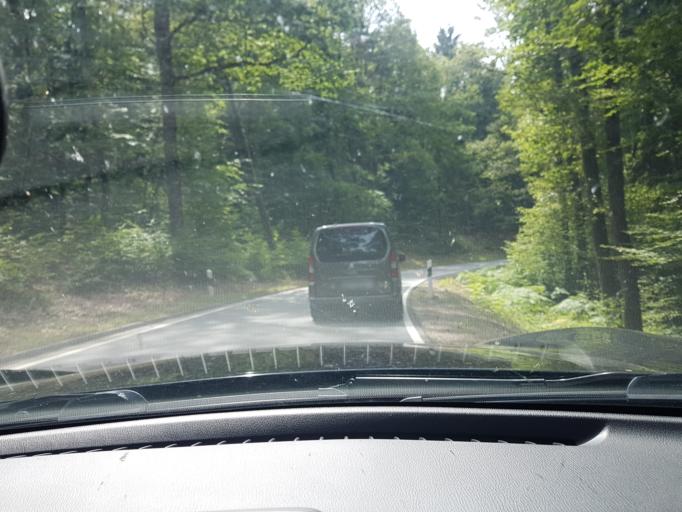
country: DE
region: Hesse
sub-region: Regierungsbezirk Darmstadt
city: Rothenberg
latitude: 49.5325
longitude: 8.9399
